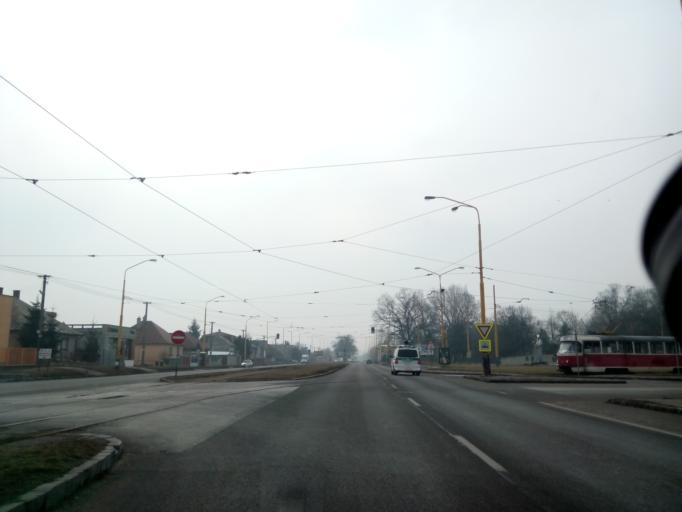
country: SK
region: Kosicky
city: Kosice
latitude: 48.6801
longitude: 21.2684
